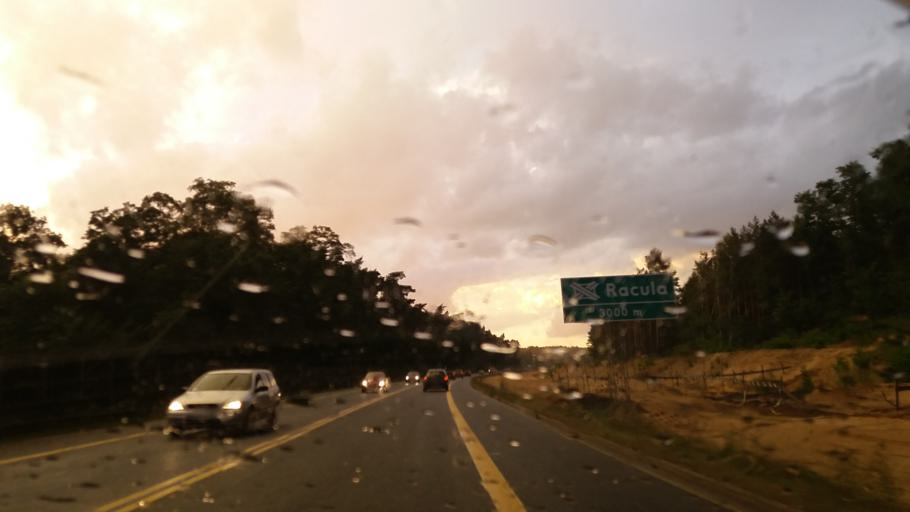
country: PL
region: Lubusz
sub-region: Zielona Gora
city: Zielona Gora
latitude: 51.8996
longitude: 15.5959
